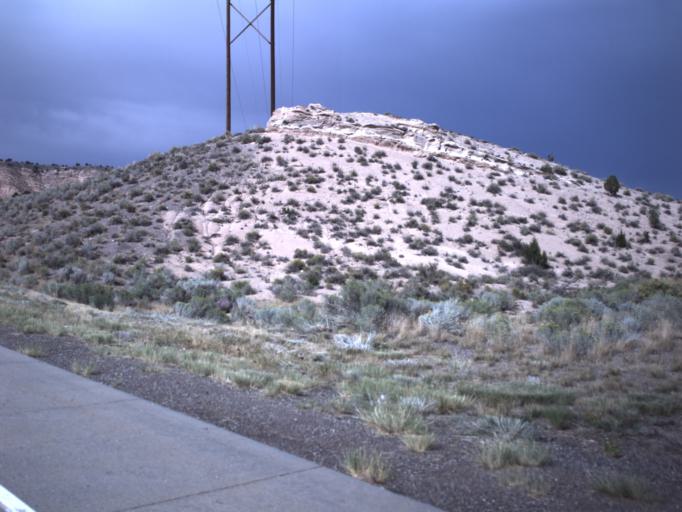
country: US
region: Utah
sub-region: Sevier County
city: Monroe
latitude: 38.6004
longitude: -112.2545
